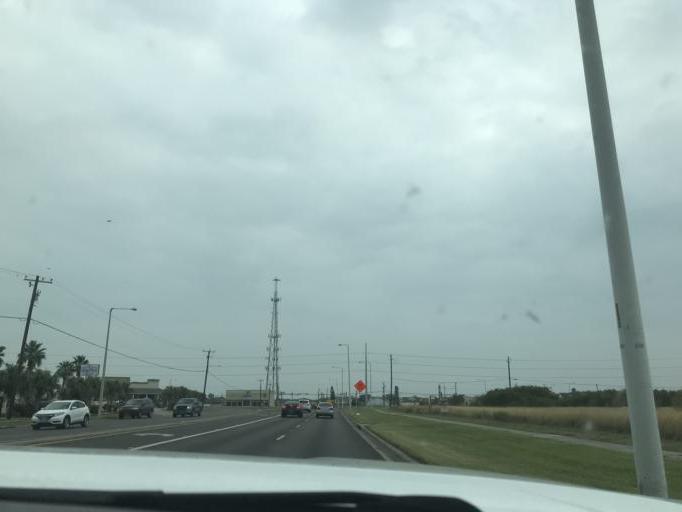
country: US
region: Texas
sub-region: Nueces County
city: Corpus Christi
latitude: 27.6725
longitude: -97.3578
